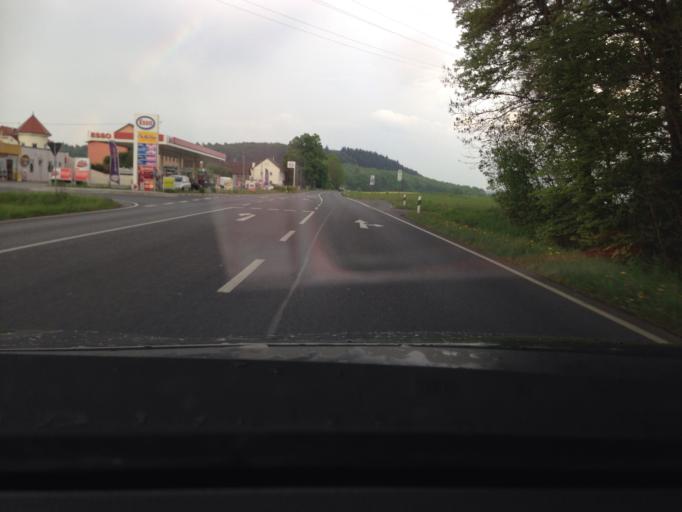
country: DE
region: Hesse
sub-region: Regierungsbezirk Giessen
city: Grossen Buseck
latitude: 50.5909
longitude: 8.7794
